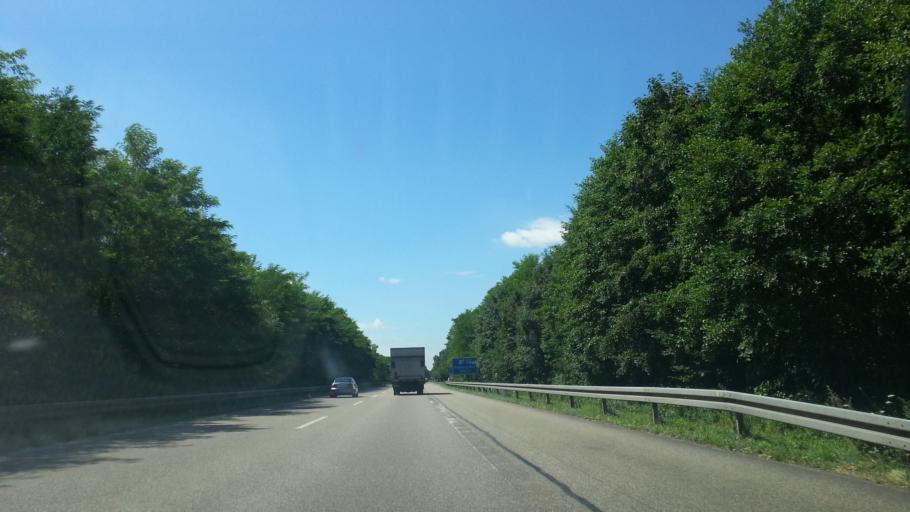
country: DE
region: Baden-Wuerttemberg
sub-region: Freiburg Region
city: Schallstadt
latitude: 47.9914
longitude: 7.7479
